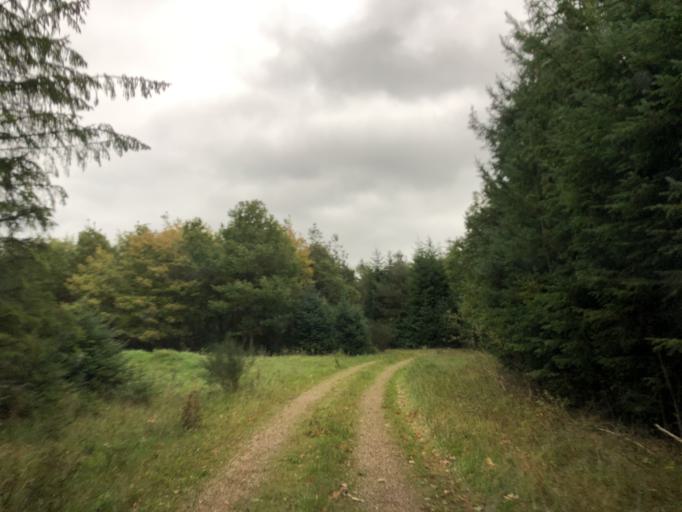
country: DK
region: Central Jutland
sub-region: Holstebro Kommune
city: Ulfborg
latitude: 56.2242
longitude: 8.4412
